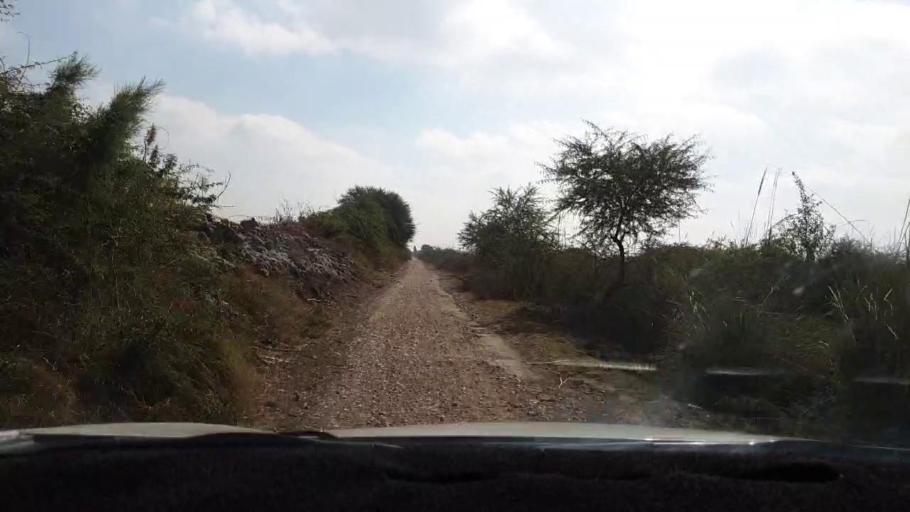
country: PK
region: Sindh
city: Berani
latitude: 25.7716
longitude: 68.9782
